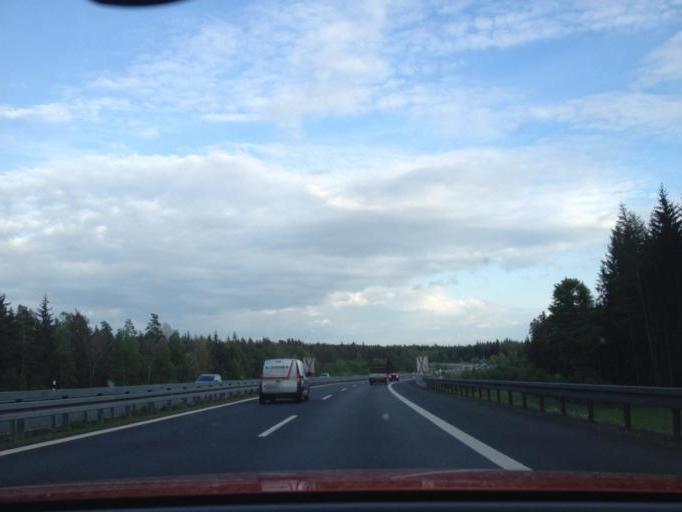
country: DE
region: Bavaria
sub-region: Upper Palatinate
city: Pechbrunn
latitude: 49.9601
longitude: 12.1899
